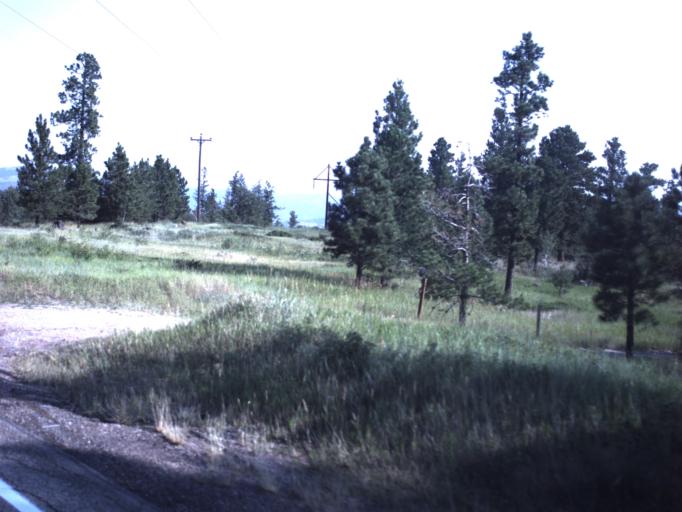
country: US
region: Utah
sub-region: Daggett County
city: Manila
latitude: 40.8591
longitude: -109.4671
